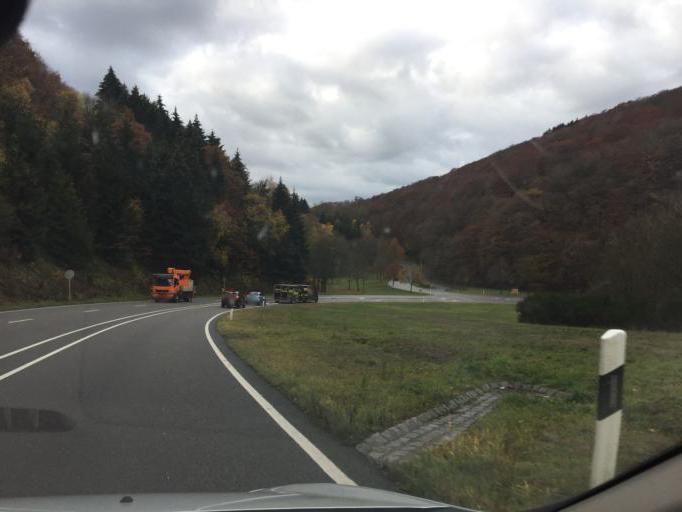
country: LU
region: Diekirch
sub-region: Canton de Wiltz
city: Esch-sur-Sure
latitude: 49.8926
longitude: 5.9546
